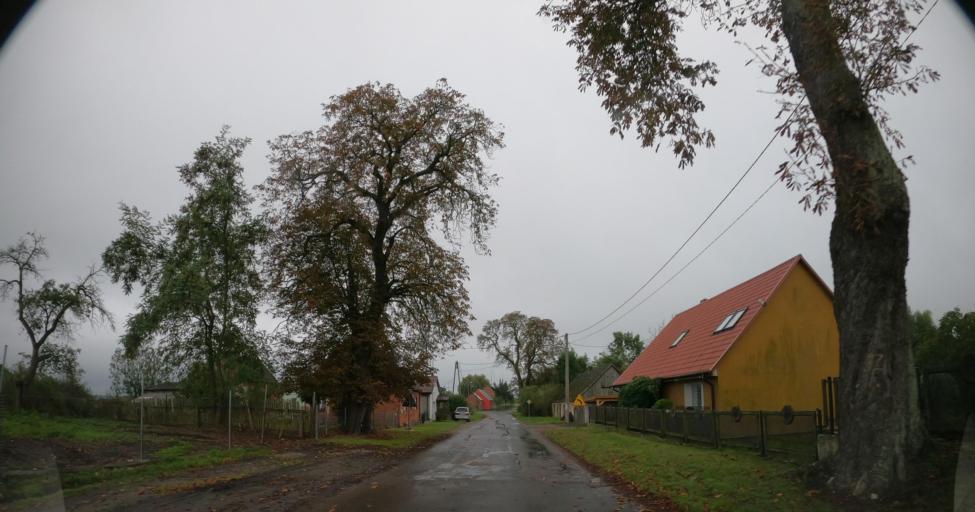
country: PL
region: West Pomeranian Voivodeship
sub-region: Powiat pyrzycki
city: Kozielice
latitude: 53.0917
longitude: 14.7712
